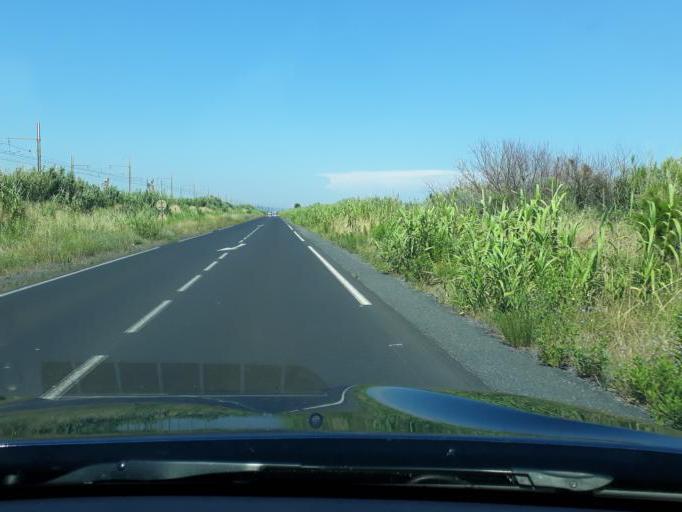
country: FR
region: Languedoc-Roussillon
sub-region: Departement de l'Herault
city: Marseillan
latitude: 43.3435
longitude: 3.5789
